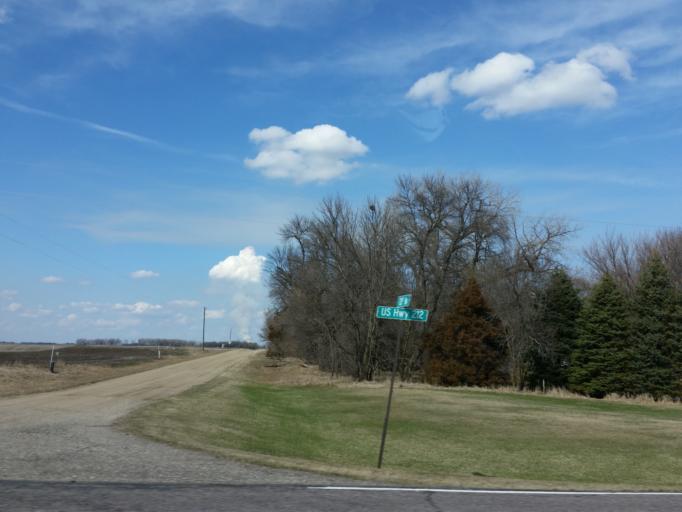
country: US
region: Minnesota
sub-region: Lac qui Parle County
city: Madison
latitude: 44.9356
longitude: -96.3946
